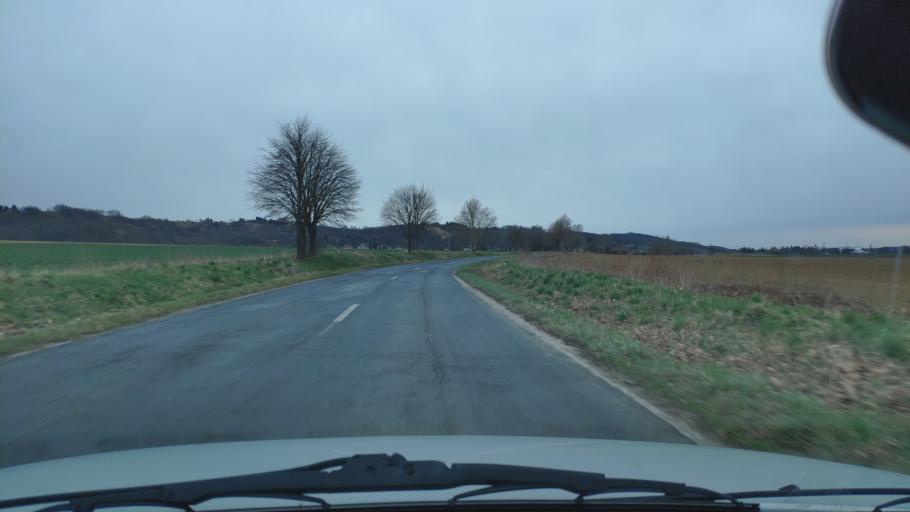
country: HU
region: Zala
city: Nagykanizsa
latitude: 46.5612
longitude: 16.9892
